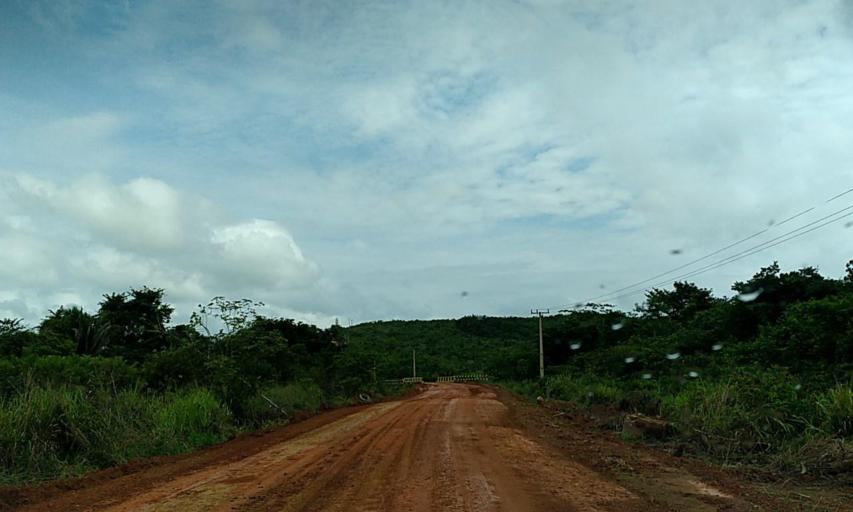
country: BR
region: Para
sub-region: Altamira
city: Altamira
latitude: -3.0874
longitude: -51.6345
